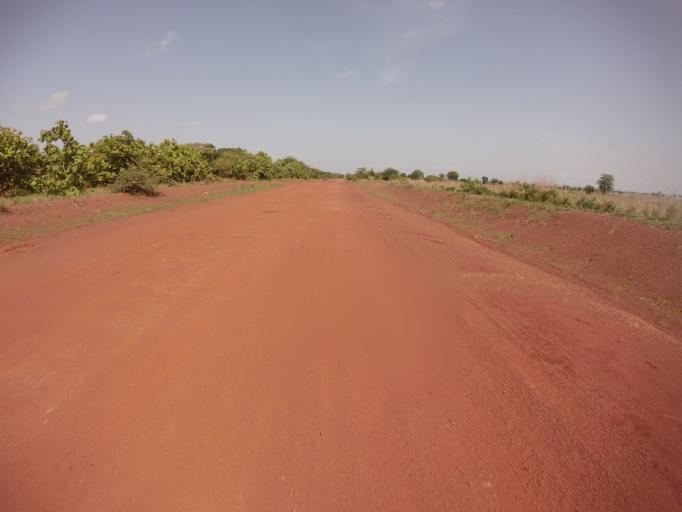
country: GH
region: Upper East
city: Bawku
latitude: 11.0017
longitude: -0.1964
